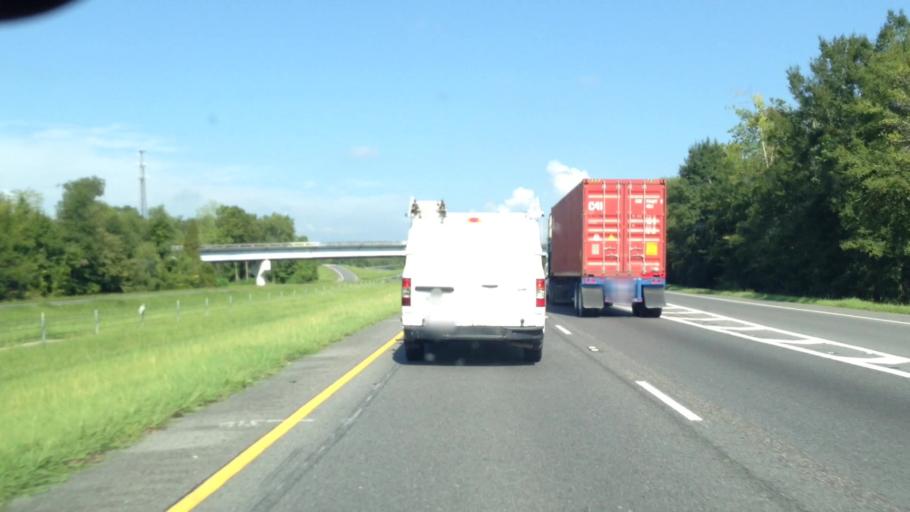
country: US
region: Louisiana
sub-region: Ascension Parish
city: Sorrento
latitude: 30.1526
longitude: -90.7992
